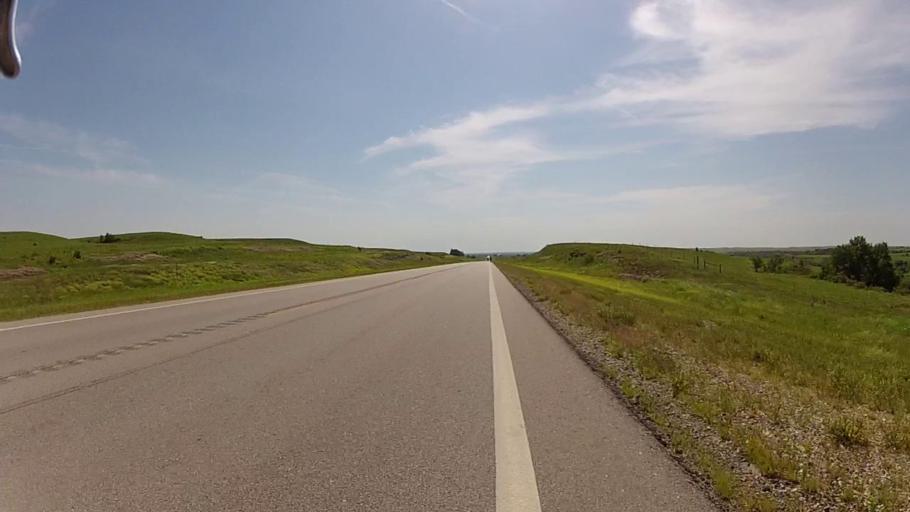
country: US
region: Kansas
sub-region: Cowley County
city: Winfield
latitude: 37.1107
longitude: -96.6382
